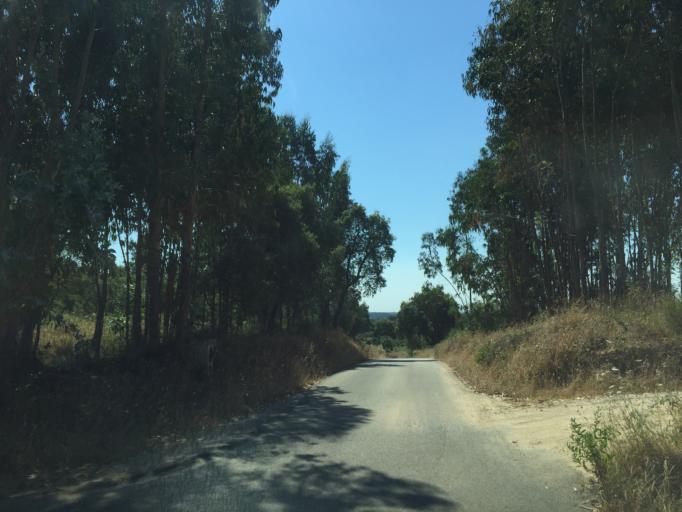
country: PT
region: Santarem
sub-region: Ferreira do Zezere
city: Ferreira do Zezere
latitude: 39.5937
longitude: -8.2883
